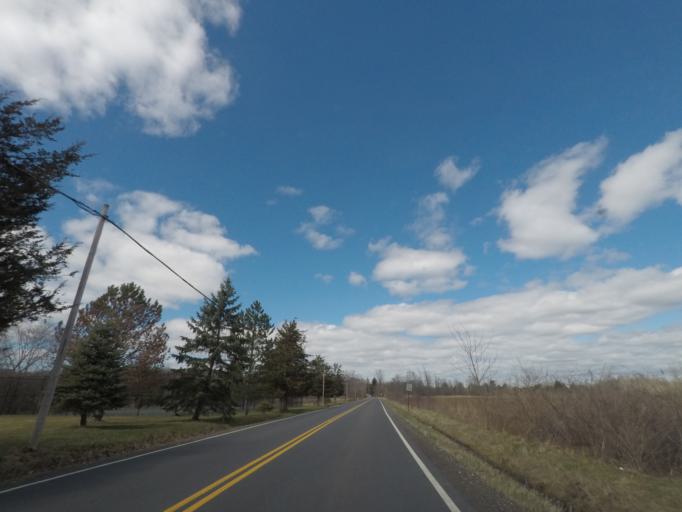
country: US
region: New York
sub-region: Albany County
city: Delmar
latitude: 42.5689
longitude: -73.8257
